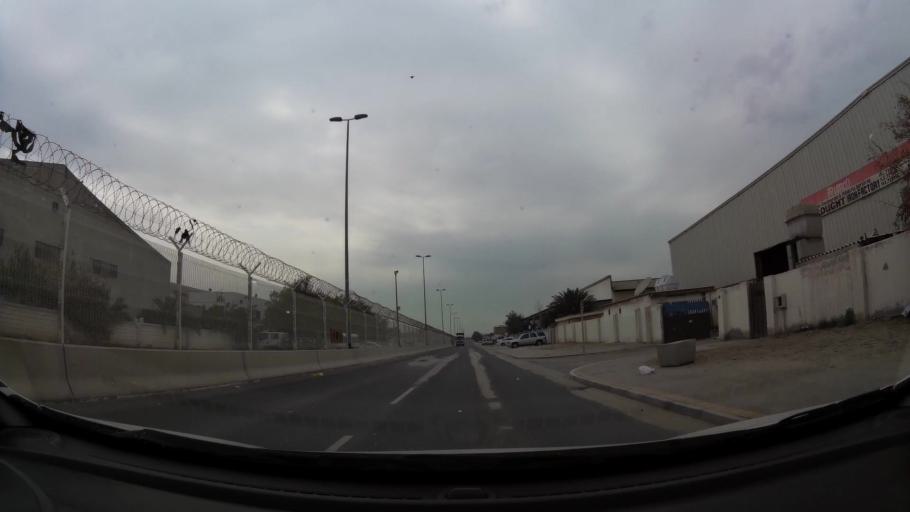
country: BH
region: Northern
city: Sitrah
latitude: 26.1819
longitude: 50.6077
